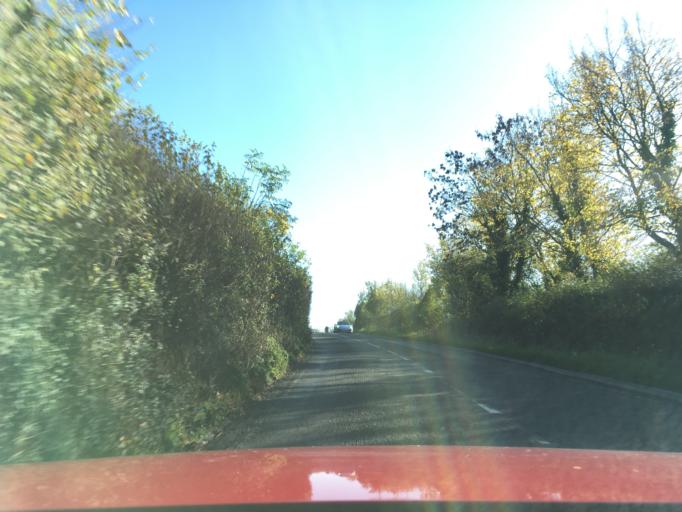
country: GB
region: England
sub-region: Somerset
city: Langport
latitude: 51.0518
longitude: -2.8374
